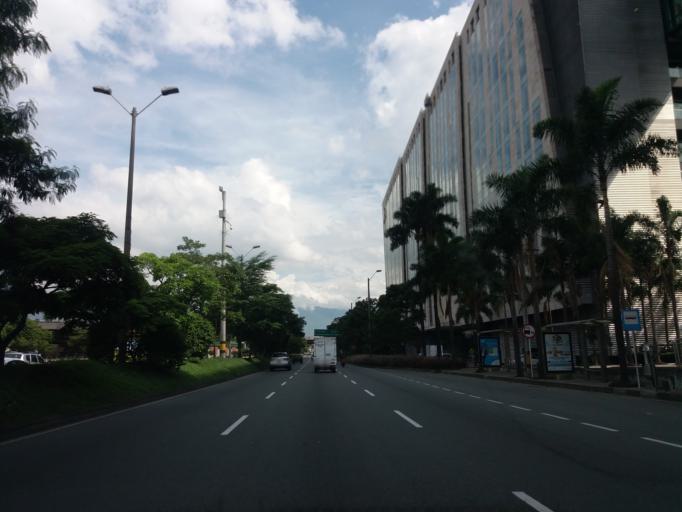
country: CO
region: Antioquia
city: Medellin
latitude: 6.2285
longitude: -75.5754
